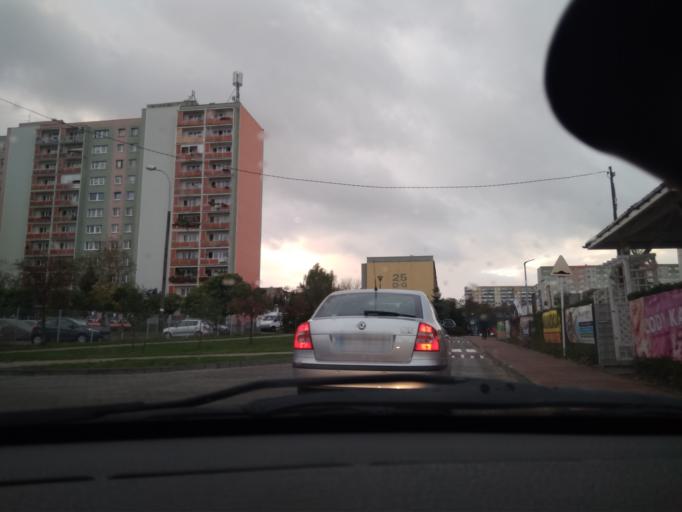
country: PL
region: Greater Poland Voivodeship
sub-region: Powiat poznanski
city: Suchy Las
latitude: 52.4644
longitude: 16.9162
